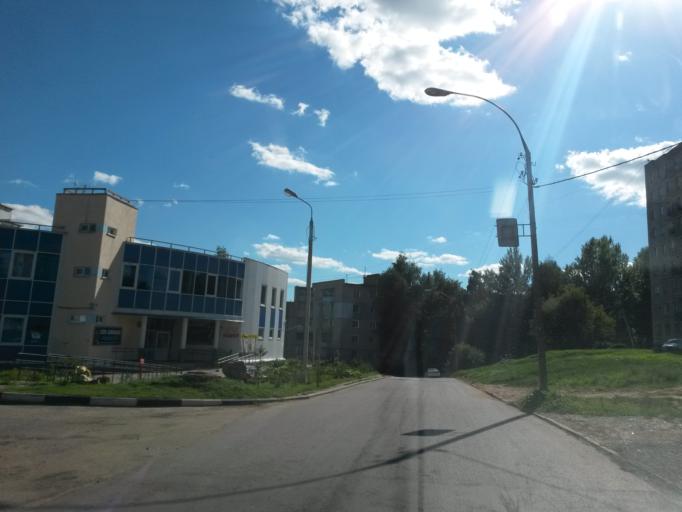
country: RU
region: Jaroslavl
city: Yaroslavl
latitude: 57.5786
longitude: 39.8605
